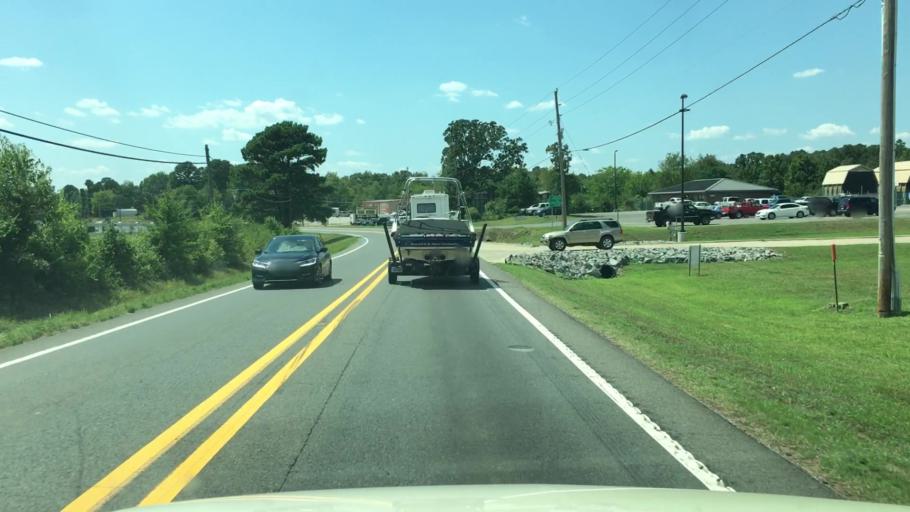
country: US
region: Arkansas
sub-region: Garland County
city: Piney
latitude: 34.5087
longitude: -93.1409
